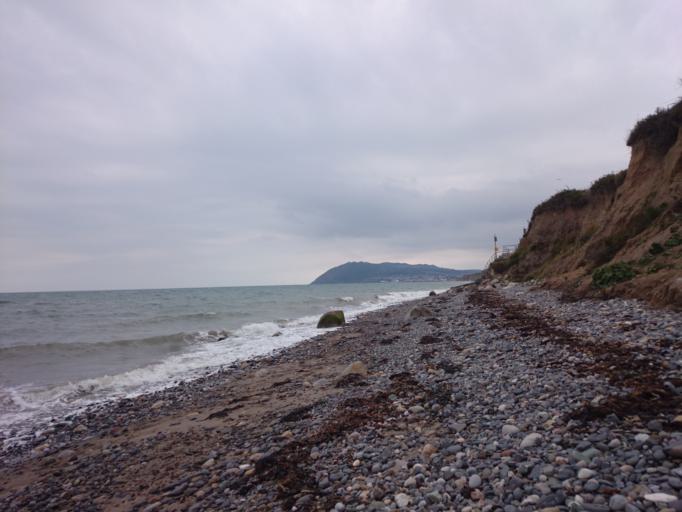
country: IE
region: Leinster
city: Shankill
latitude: 53.2312
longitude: -6.1084
